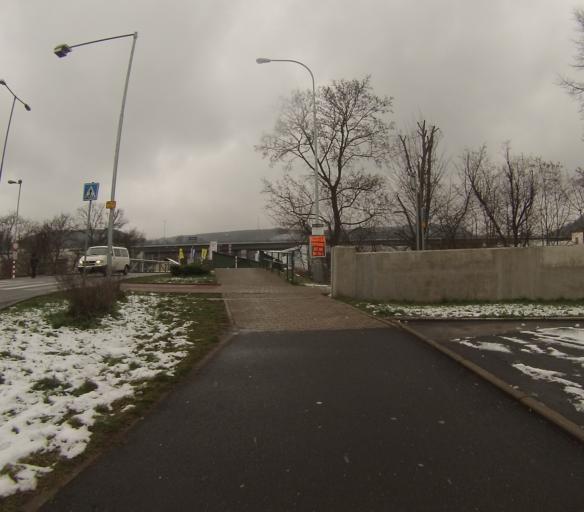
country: CZ
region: Ustecky
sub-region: Okres Decin
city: Decin
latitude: 50.7754
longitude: 14.2181
